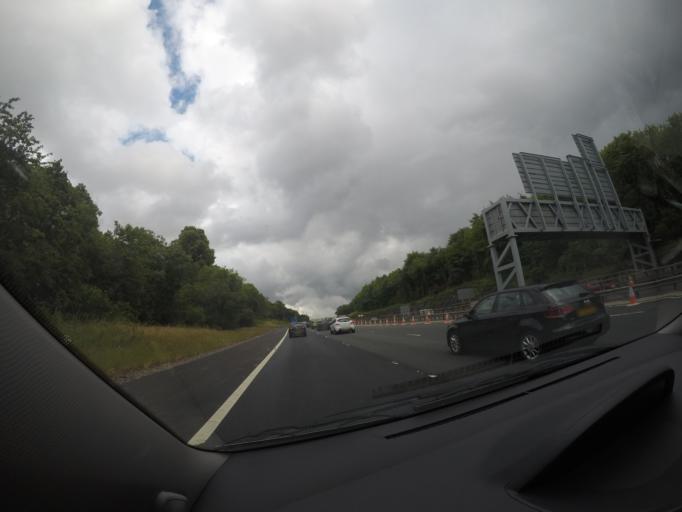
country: GB
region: Scotland
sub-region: South Lanarkshire
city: Uddingston
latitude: 55.8279
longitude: -4.0885
